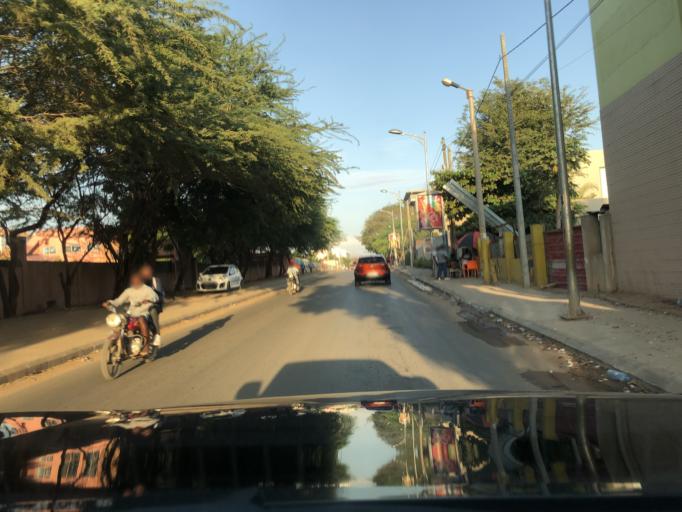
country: AO
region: Luanda
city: Luanda
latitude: -8.9469
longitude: 13.1639
